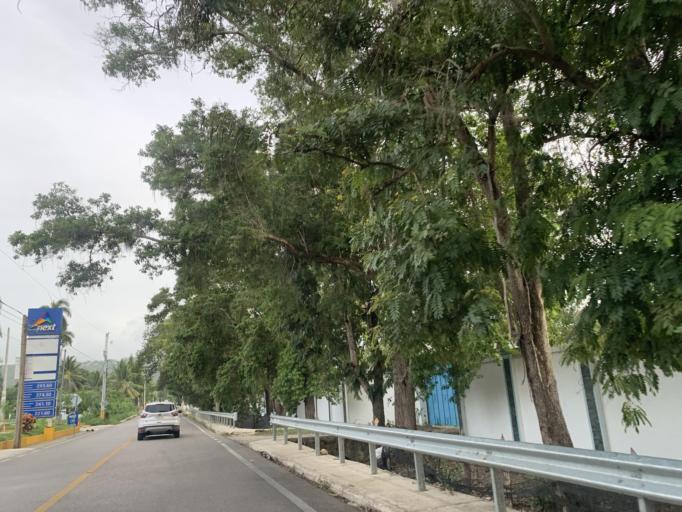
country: DO
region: Puerto Plata
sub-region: Puerto Plata
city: Puerto Plata
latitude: 19.7035
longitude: -70.6246
